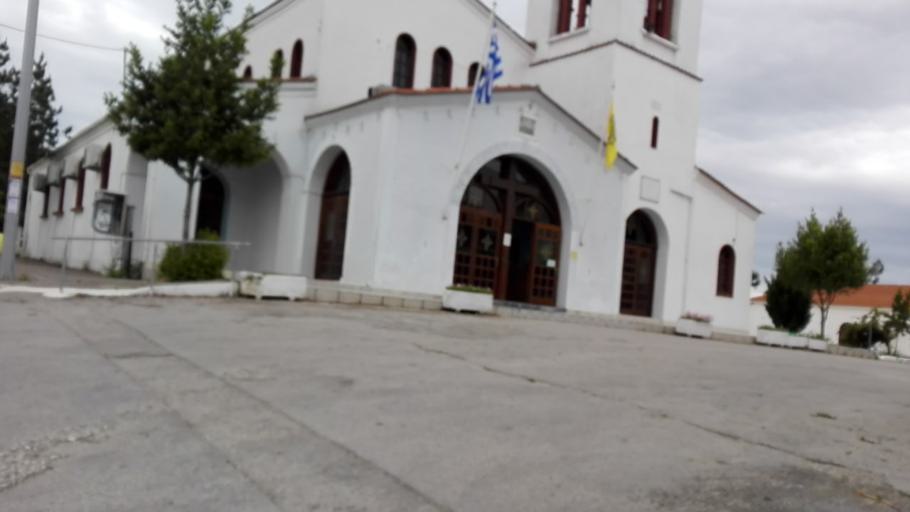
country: GR
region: East Macedonia and Thrace
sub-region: Nomos Kavalas
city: Limenaria
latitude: 40.6274
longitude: 24.5789
